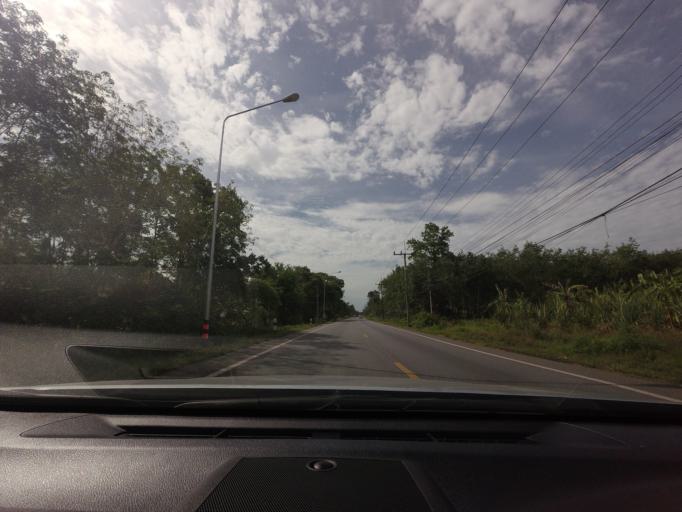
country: TH
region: Songkhla
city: Khlong Hoi Khong
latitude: 6.8933
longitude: 100.4145
